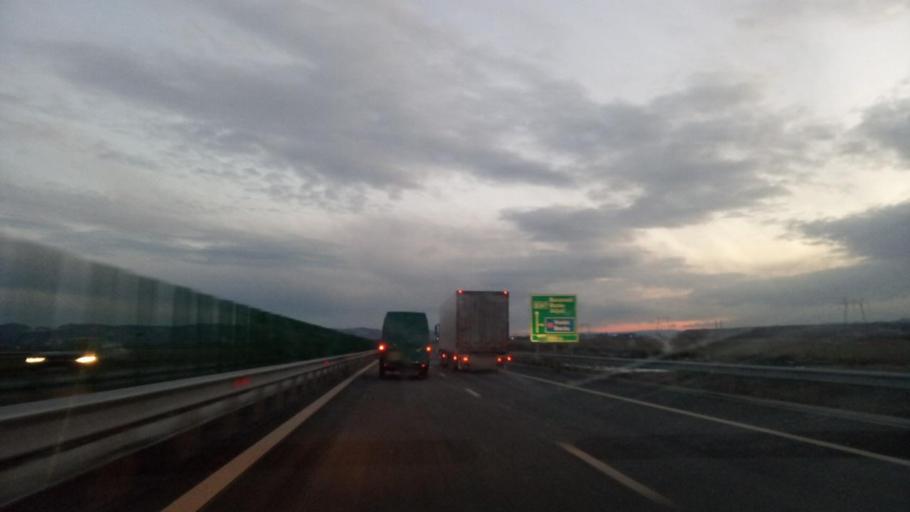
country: RO
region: Bacau
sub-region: Comuna Saucesti
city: Saucesti
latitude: 46.6151
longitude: 26.9574
